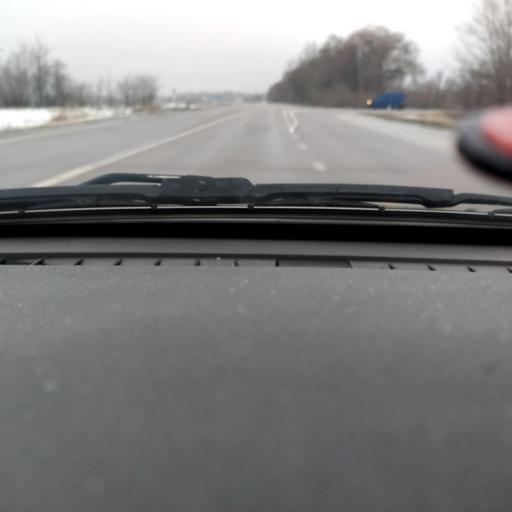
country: RU
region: Voronezj
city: Novaya Usman'
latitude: 51.5894
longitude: 39.3390
